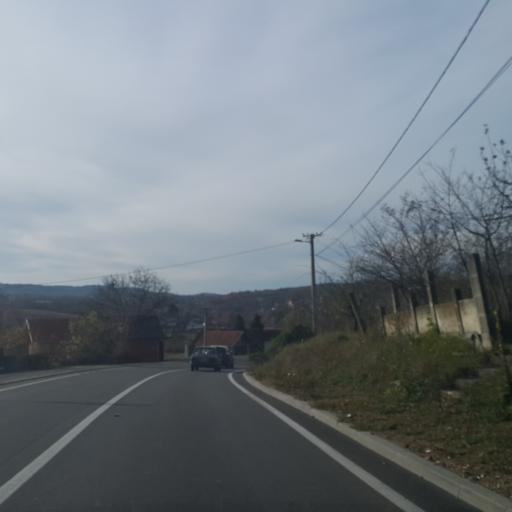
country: RS
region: Central Serbia
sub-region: Sumadijski Okrug
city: Arangelovac
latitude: 44.3342
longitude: 20.4671
